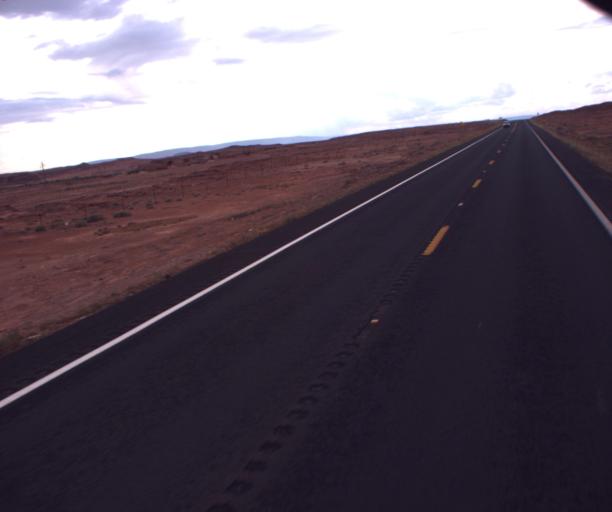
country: US
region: Arizona
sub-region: Coconino County
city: Tuba City
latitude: 36.1035
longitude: -111.2819
